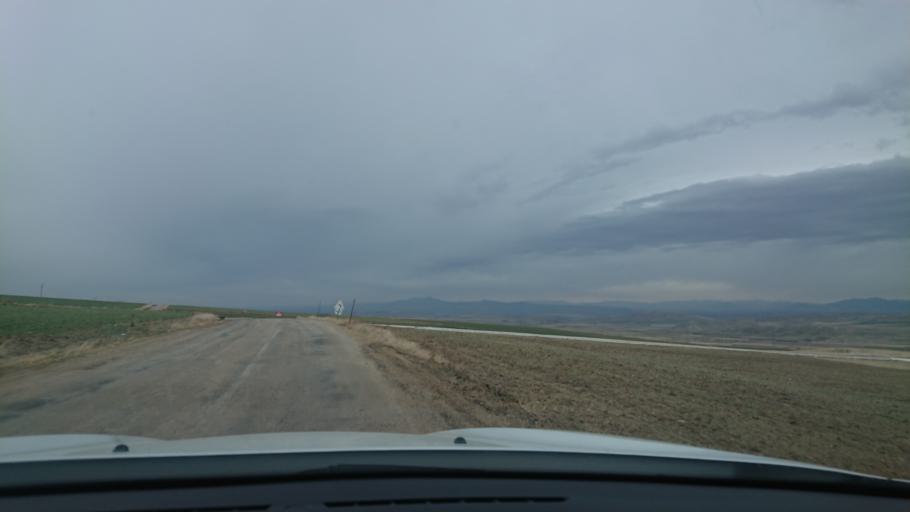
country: TR
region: Aksaray
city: Agacoren
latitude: 38.9430
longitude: 33.9115
